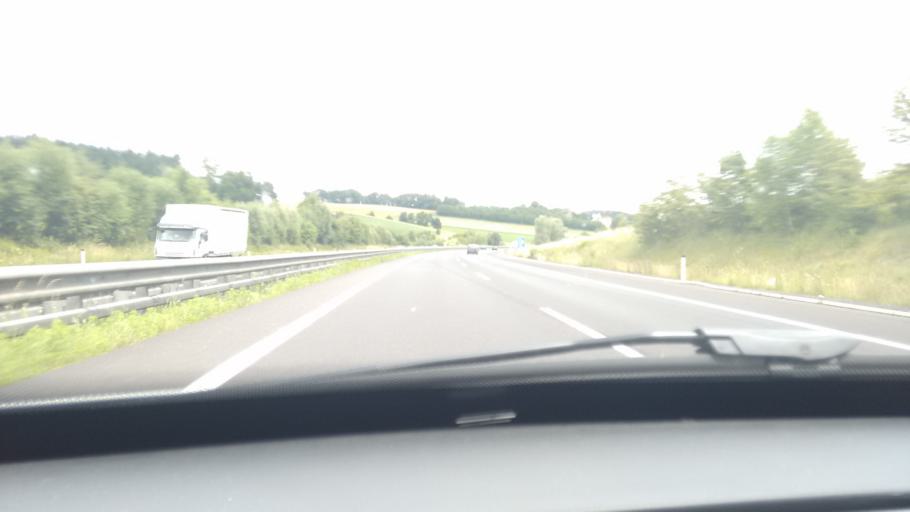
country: AT
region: Upper Austria
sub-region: Wels-Land
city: Offenhausen
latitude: 48.1860
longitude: 13.7988
